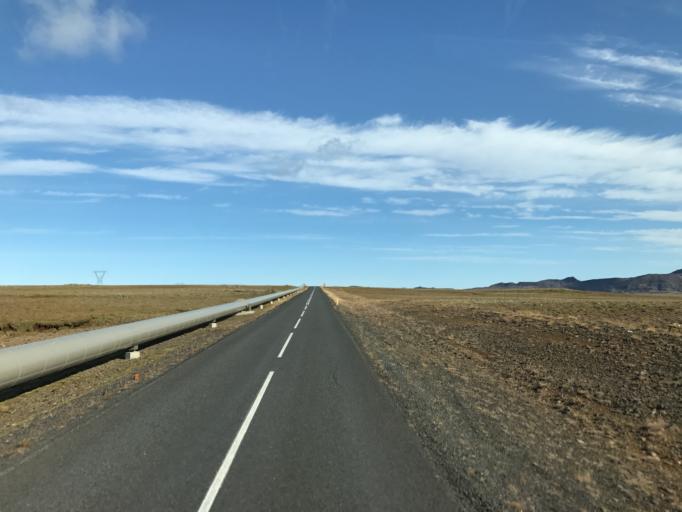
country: IS
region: South
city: THorlakshoefn
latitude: 64.1197
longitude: -21.4260
